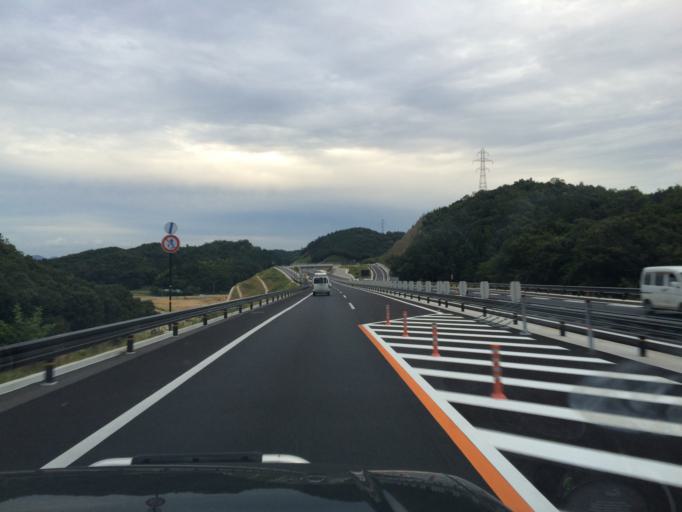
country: JP
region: Tottori
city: Tottori
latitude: 35.4926
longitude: 134.1464
